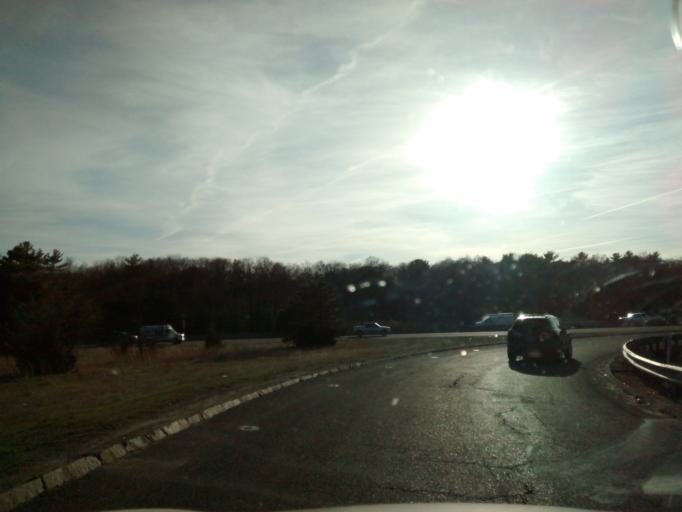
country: US
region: Massachusetts
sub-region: Norfolk County
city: Avon
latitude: 42.1235
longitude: -71.0606
